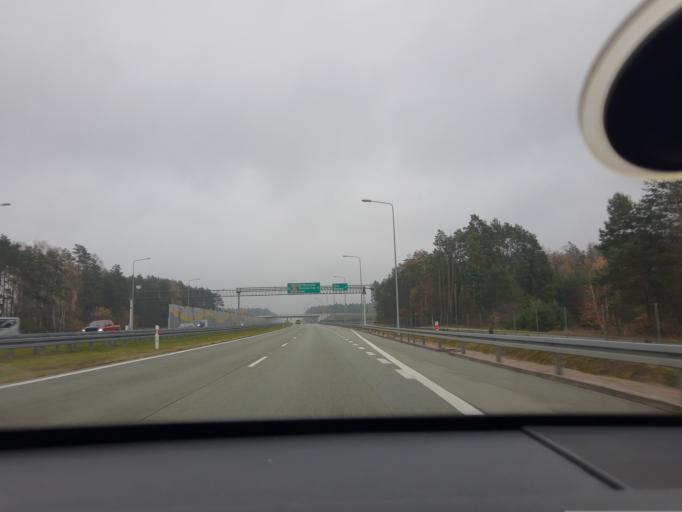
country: PL
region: Lodz Voivodeship
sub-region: Powiat laski
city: Lask
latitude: 51.5711
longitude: 19.1724
